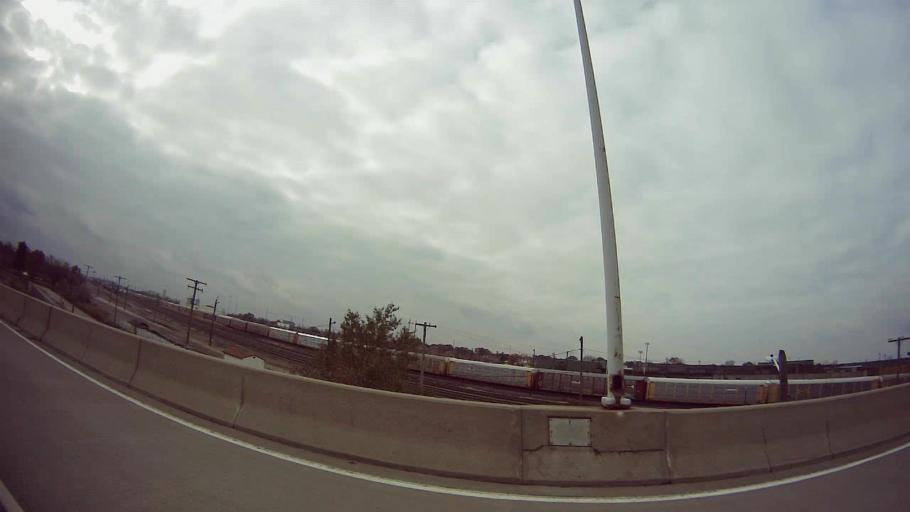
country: US
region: Michigan
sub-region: Wayne County
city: Hamtramck
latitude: 42.4037
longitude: -83.0380
